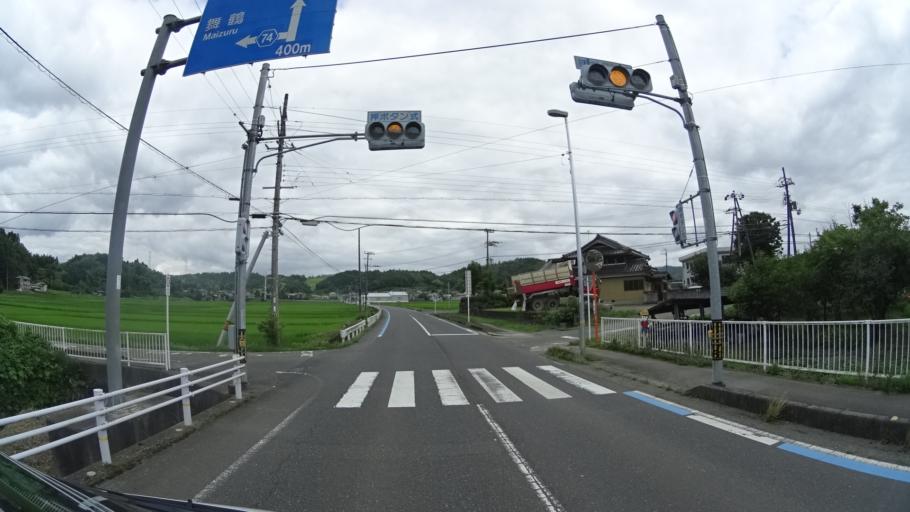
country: JP
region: Kyoto
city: Ayabe
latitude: 35.3187
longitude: 135.2640
